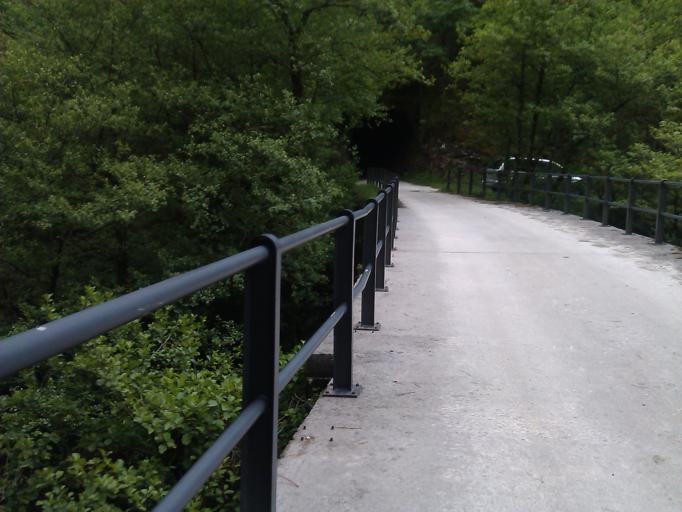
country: ES
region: Basque Country
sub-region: Provincia de Guipuzcoa
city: Berastegui
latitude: 43.1344
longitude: -1.9437
